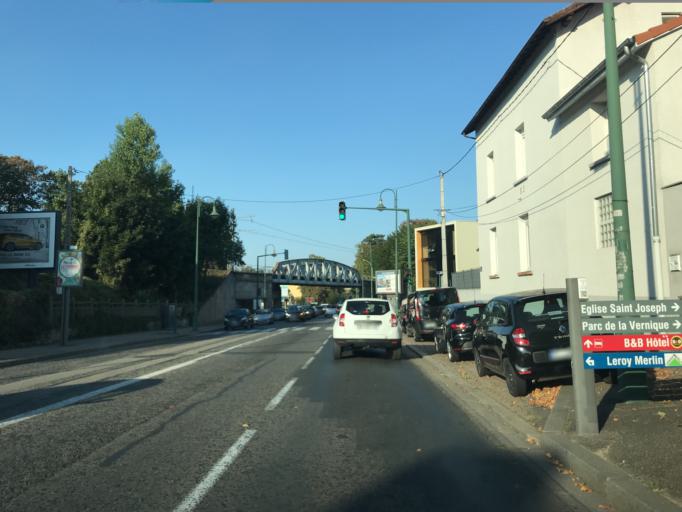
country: FR
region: Rhone-Alpes
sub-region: Departement du Rhone
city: Tassin-la-Demi-Lune
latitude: 45.7677
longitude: 4.7858
